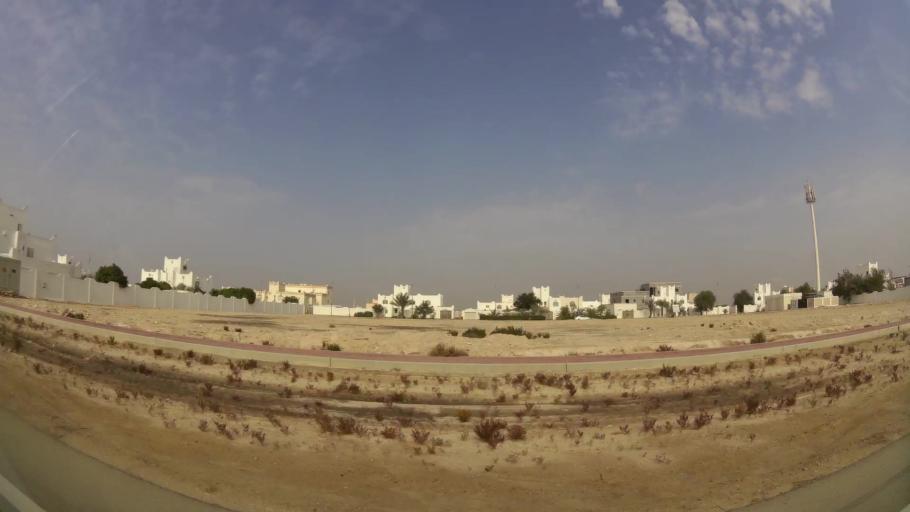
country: AE
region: Abu Dhabi
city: Abu Dhabi
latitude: 24.6611
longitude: 54.7703
